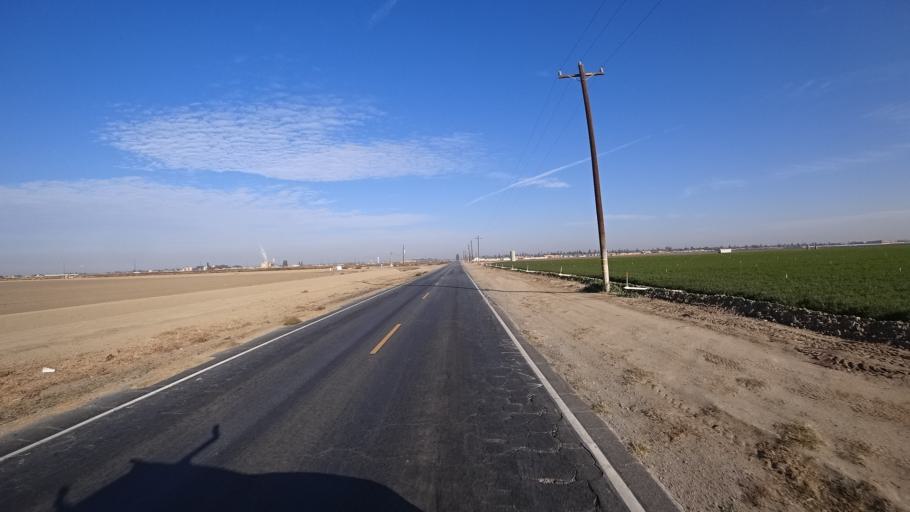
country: US
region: California
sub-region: Kern County
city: Greenfield
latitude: 35.2874
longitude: -119.0922
